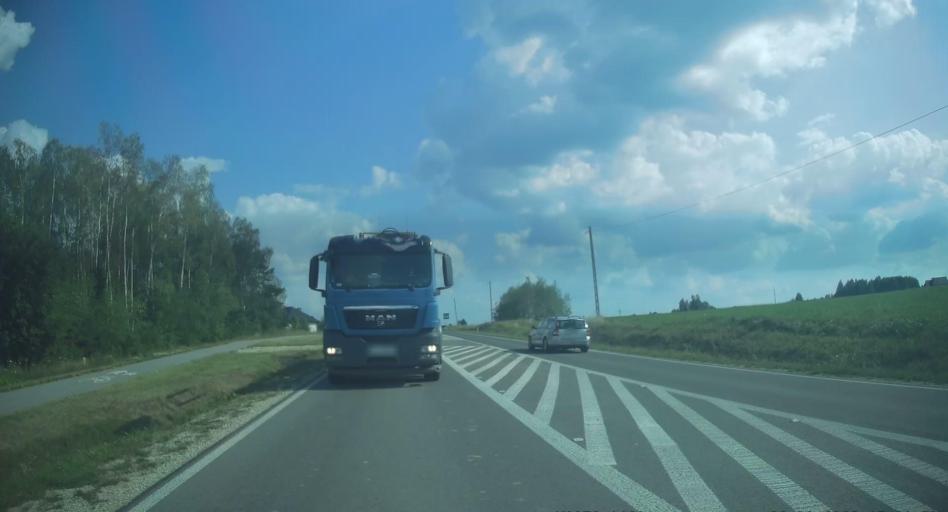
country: PL
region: Swietokrzyskie
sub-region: Powiat konecki
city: Radoszyce
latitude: 51.0368
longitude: 20.2846
